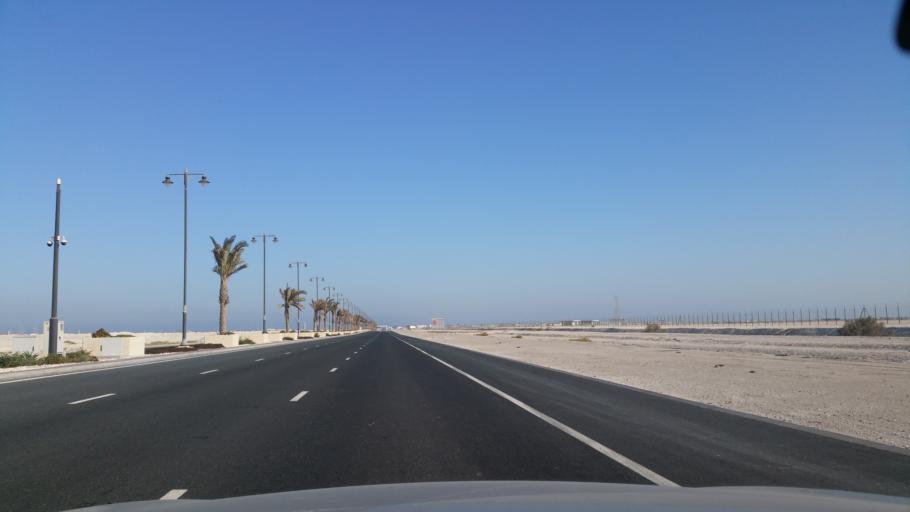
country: QA
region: Al Wakrah
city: Umm Sa'id
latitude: 25.0592
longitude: 51.5903
